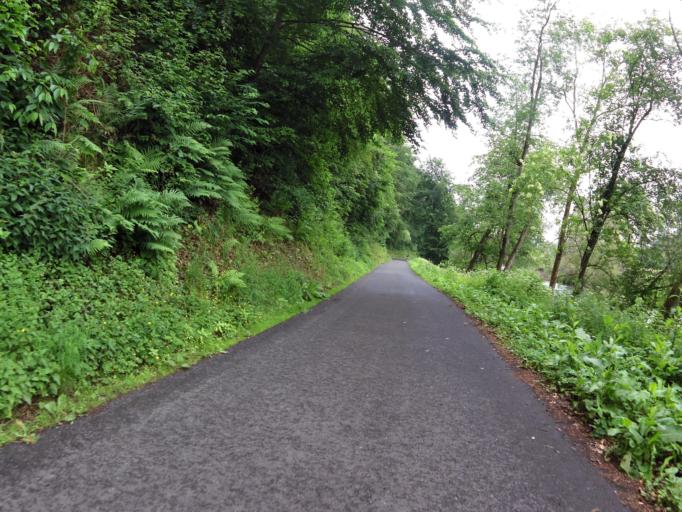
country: DE
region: Hesse
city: Breitenbach
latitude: 50.9649
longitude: 9.7739
